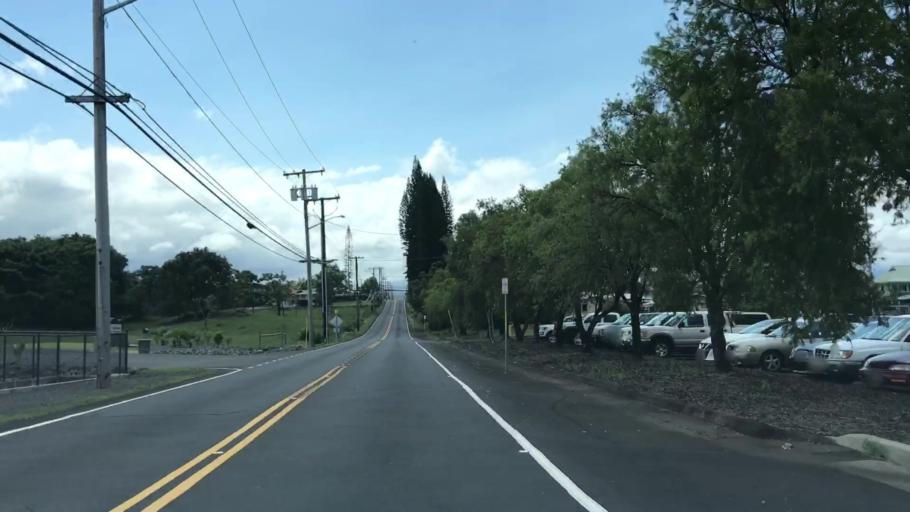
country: US
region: Hawaii
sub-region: Hawaii County
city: Hilo
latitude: 19.6739
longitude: -155.0777
